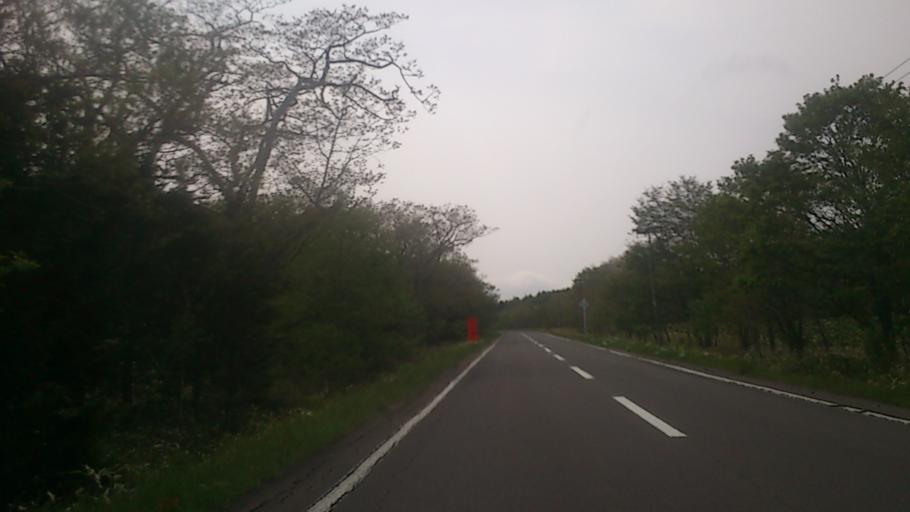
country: JP
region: Hokkaido
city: Nemuro
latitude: 43.2077
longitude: 145.3402
